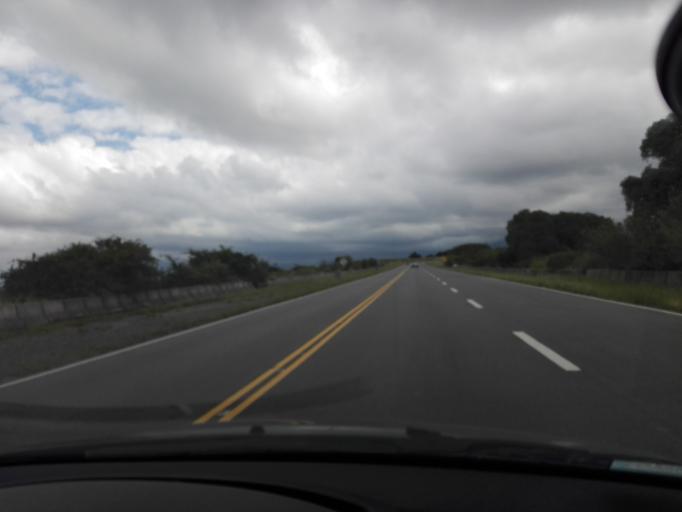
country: AR
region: Cordoba
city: Cuesta Blanca
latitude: -31.5839
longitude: -64.6135
